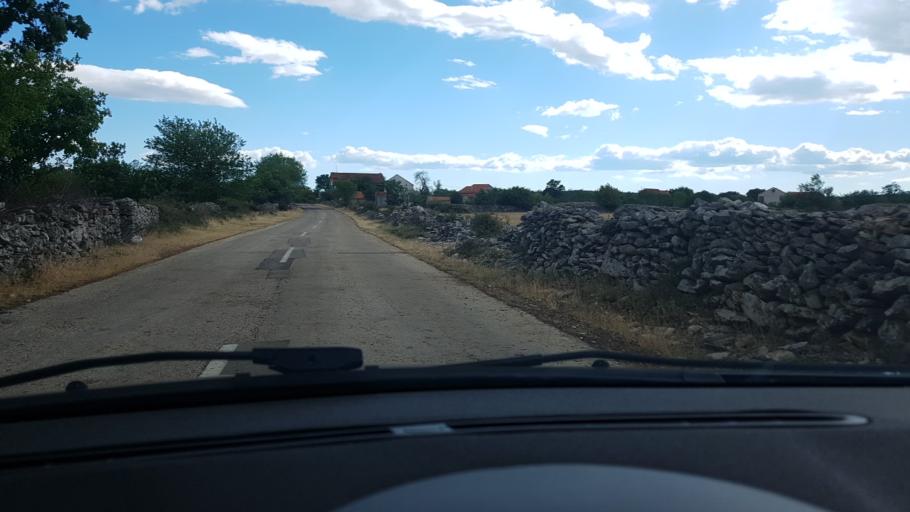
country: HR
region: Sibensko-Kniniska
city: Kistanje
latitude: 44.0583
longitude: 15.9279
